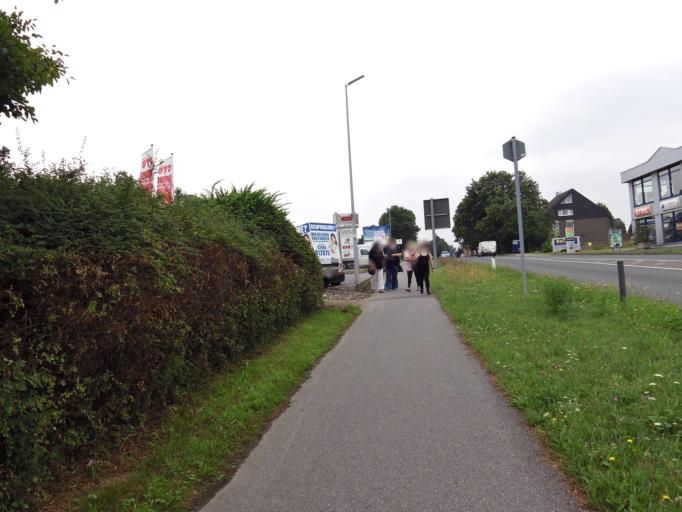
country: DE
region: North Rhine-Westphalia
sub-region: Regierungsbezirk Koln
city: Alsdorf
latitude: 50.8877
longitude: 6.1730
